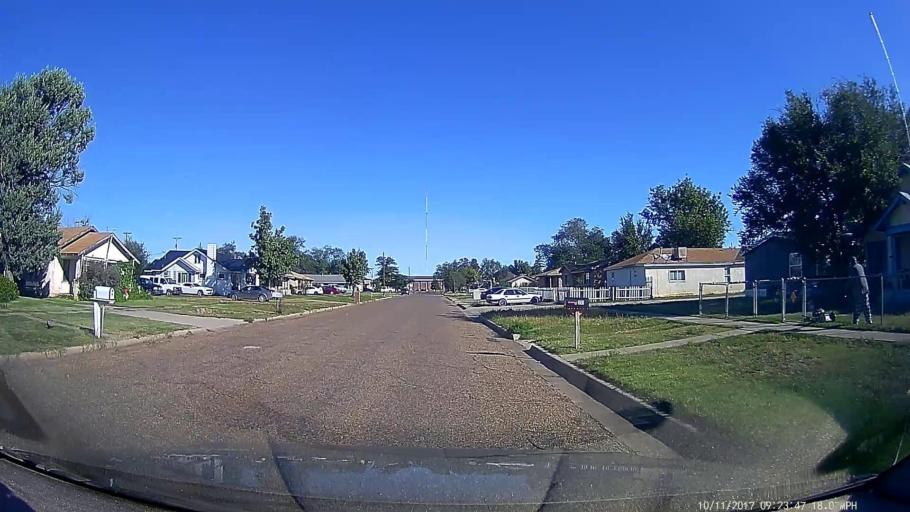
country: US
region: New Mexico
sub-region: Curry County
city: Clovis
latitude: 34.4099
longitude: -103.2077
